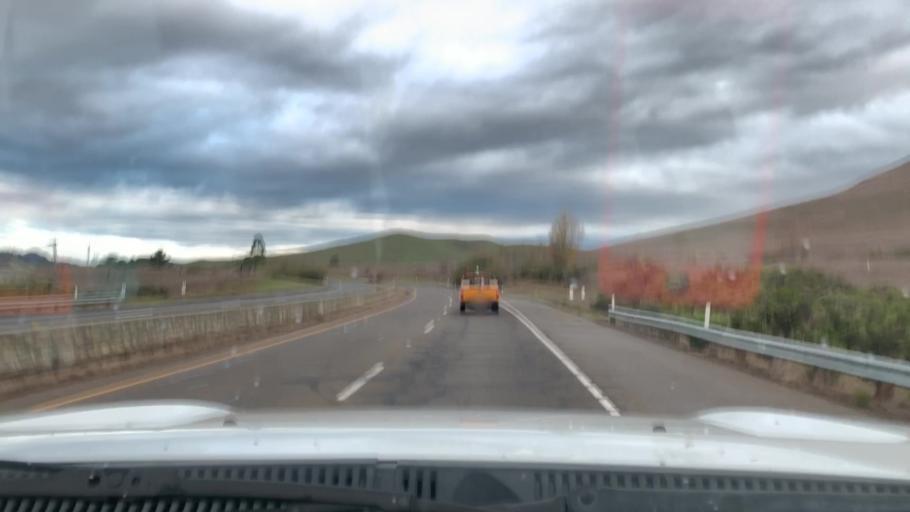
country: US
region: California
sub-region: San Luis Obispo County
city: Los Osos
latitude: 35.3511
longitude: -120.7743
